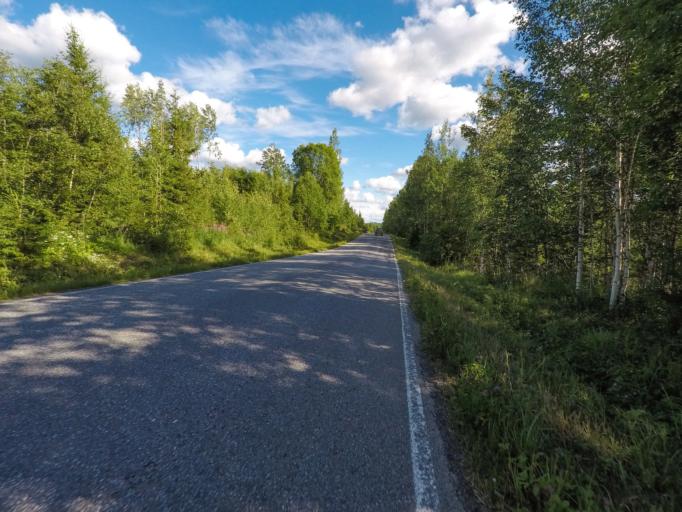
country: FI
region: South Karelia
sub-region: Imatra
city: Imatra
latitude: 61.1315
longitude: 28.6613
